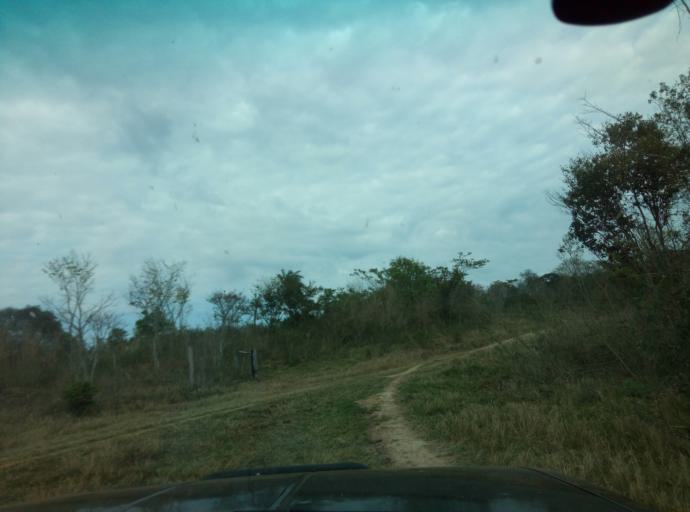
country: PY
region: Caaguazu
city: Doctor Cecilio Baez
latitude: -25.1999
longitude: -56.1276
